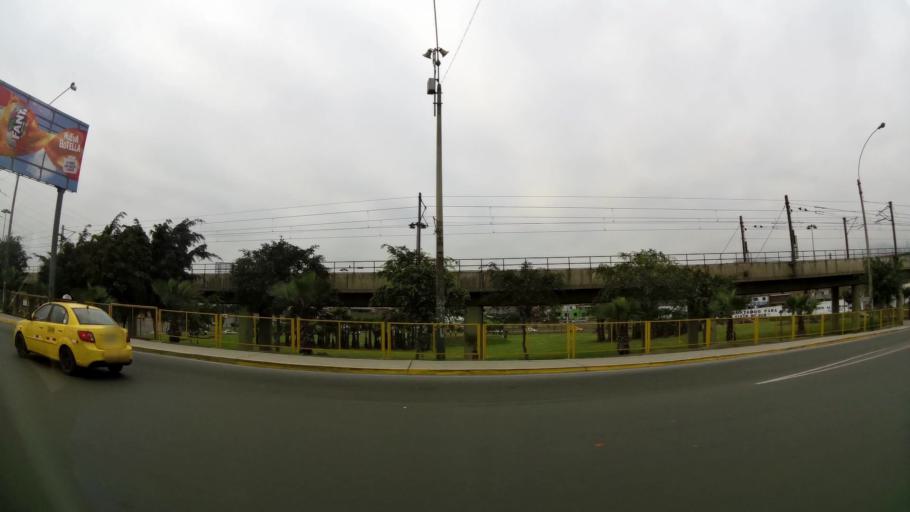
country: PE
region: Lima
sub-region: Lima
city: Surco
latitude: -12.1500
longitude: -76.9823
